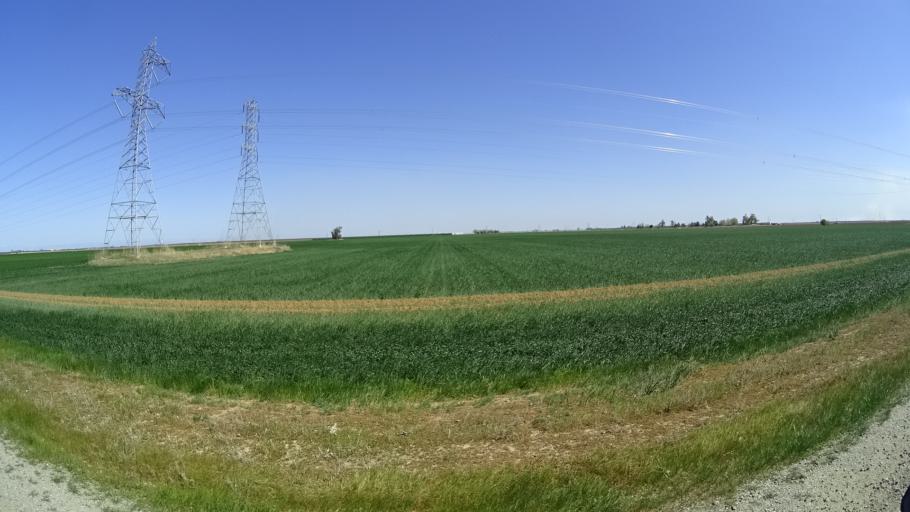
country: US
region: California
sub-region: Glenn County
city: Willows
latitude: 39.4686
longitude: -122.2868
